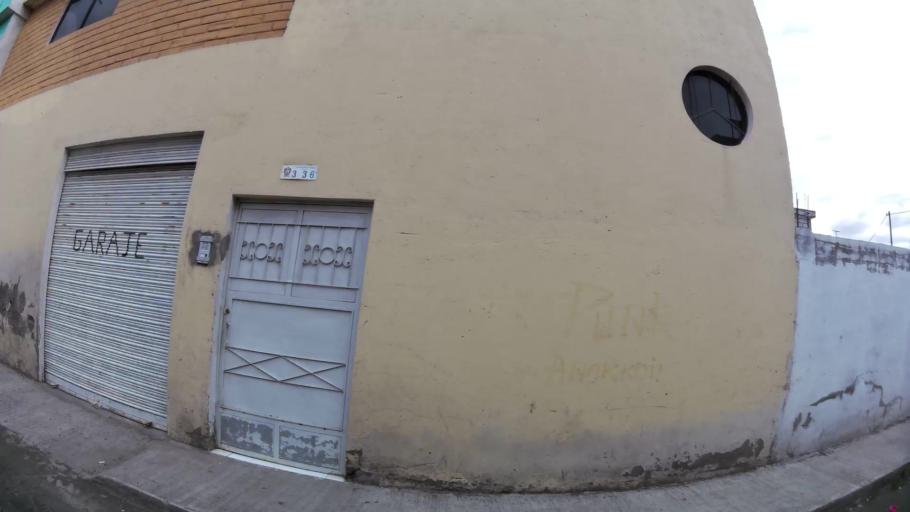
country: EC
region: Cotopaxi
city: Latacunga
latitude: -0.9316
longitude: -78.6238
